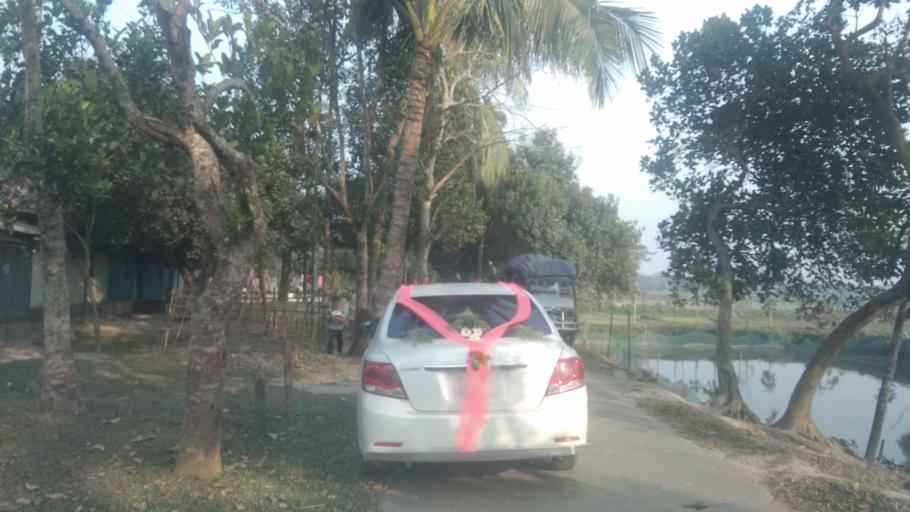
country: BD
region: Dhaka
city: Netrakona
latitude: 24.7754
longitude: 90.6057
